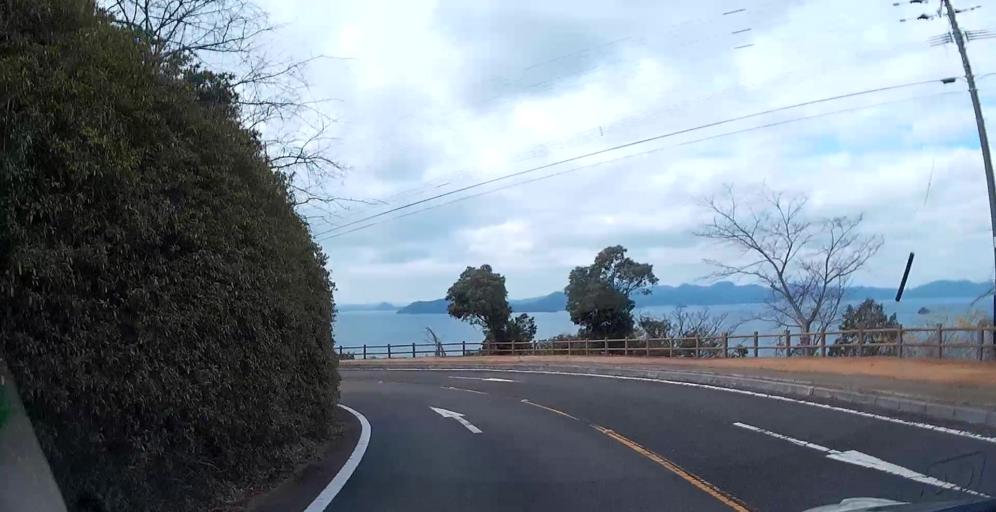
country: JP
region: Kumamoto
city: Yatsushiro
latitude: 32.3682
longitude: 130.4964
